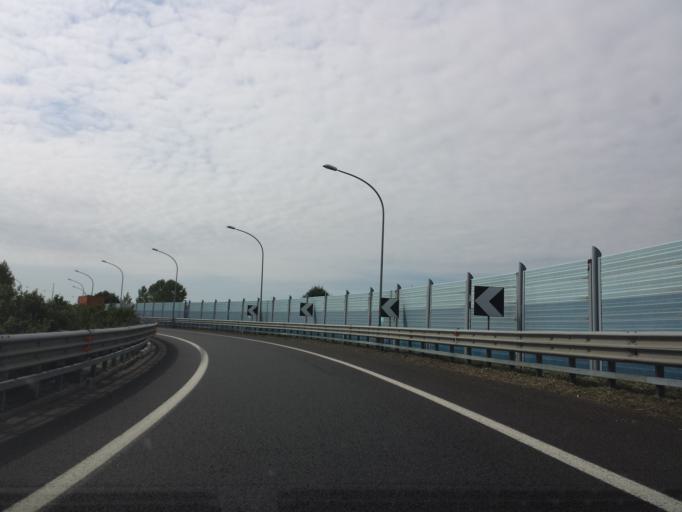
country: IT
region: Veneto
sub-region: Provincia di Venezia
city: Mestre
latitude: 45.4799
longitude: 12.2159
